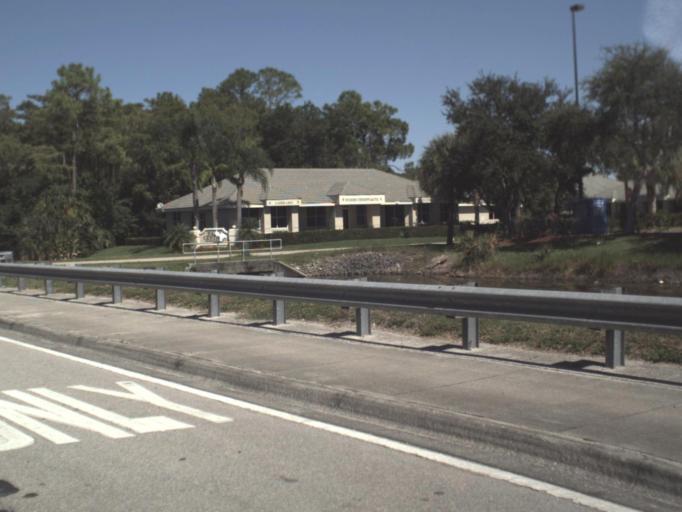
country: US
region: Florida
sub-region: Collier County
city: Pine Ridge
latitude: 26.2130
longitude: -81.7683
